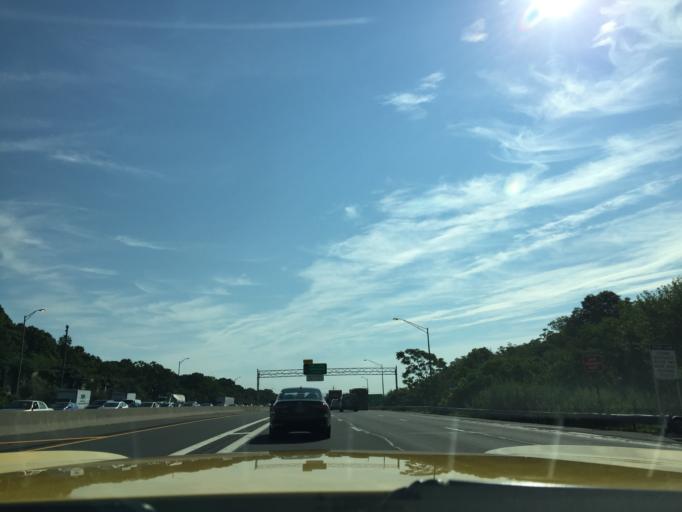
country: US
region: New York
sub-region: Suffolk County
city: Dix Hills
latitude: 40.8005
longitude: -73.3347
